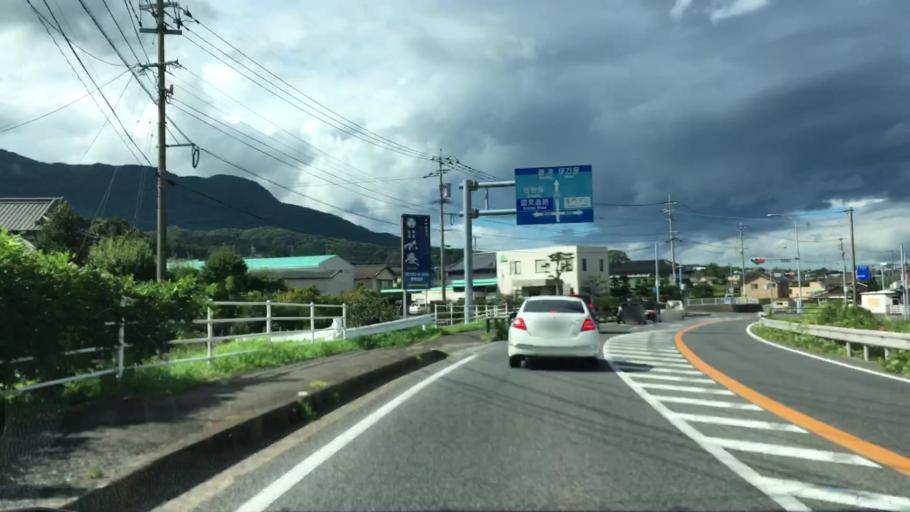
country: JP
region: Saga Prefecture
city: Imaricho-ko
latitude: 33.2245
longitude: 129.8472
